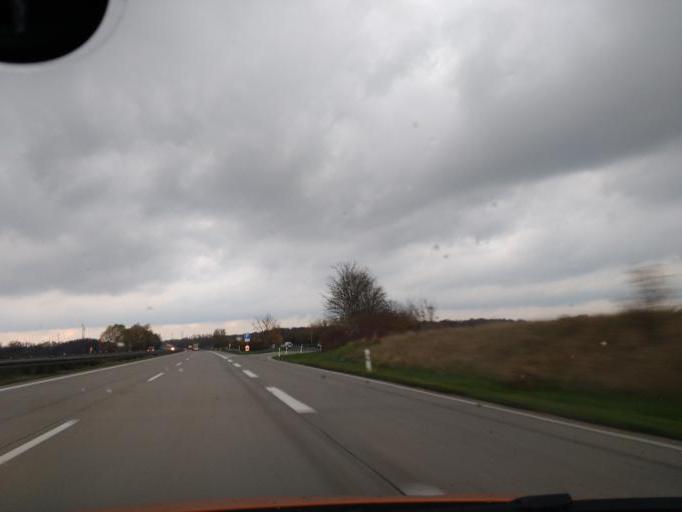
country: DE
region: Brandenburg
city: Gerdshagen
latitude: 53.1959
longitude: 12.2770
